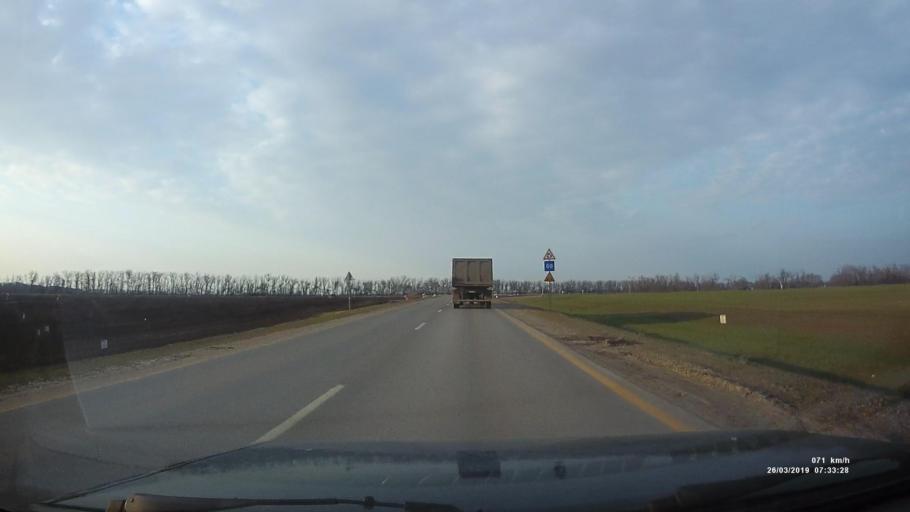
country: RU
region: Rostov
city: Novobessergenovka
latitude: 47.2149
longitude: 38.7700
